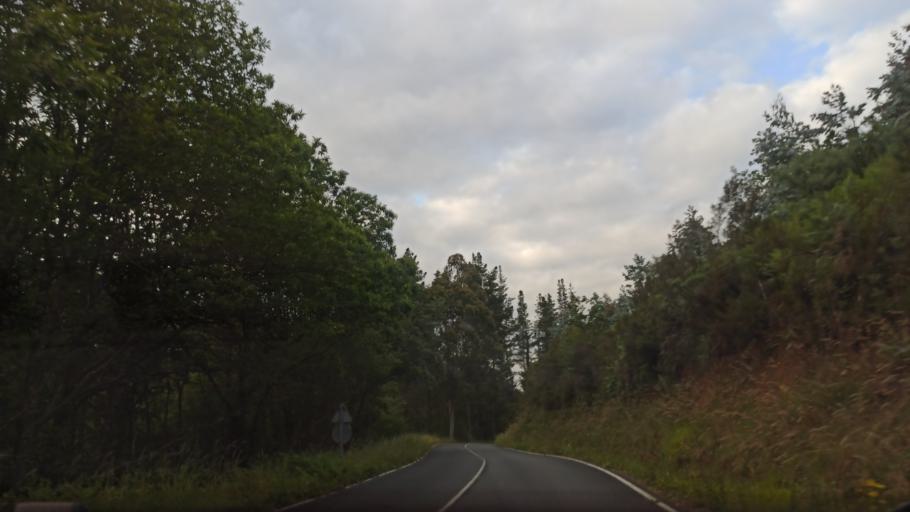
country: ES
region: Galicia
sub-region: Provincia da Coruna
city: Santiso
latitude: 42.8150
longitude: -8.1402
